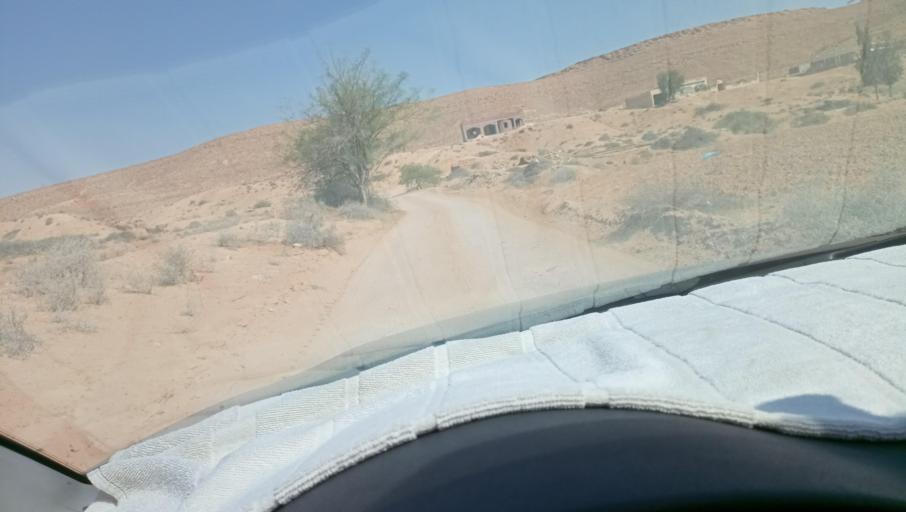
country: TN
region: Tataouine
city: Tataouine
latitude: 32.9857
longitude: 10.3910
